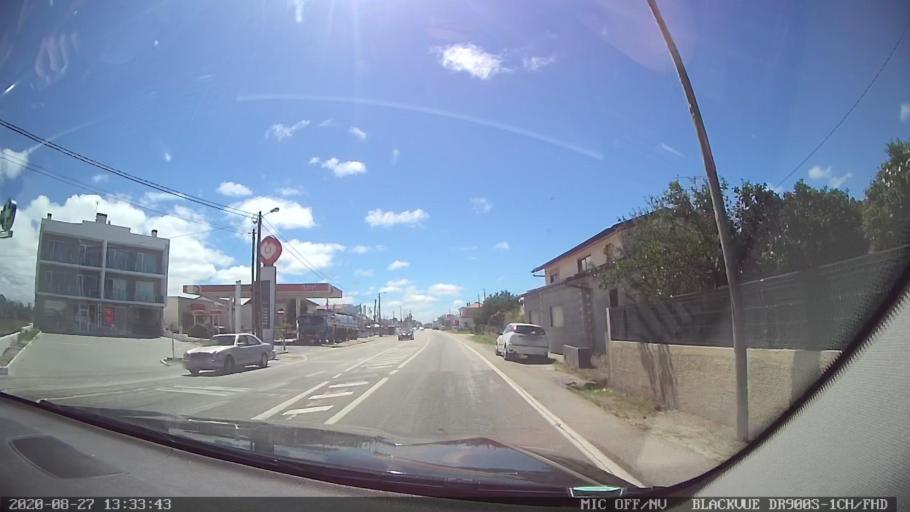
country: PT
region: Coimbra
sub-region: Mira
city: Mira
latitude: 40.4765
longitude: -8.6956
